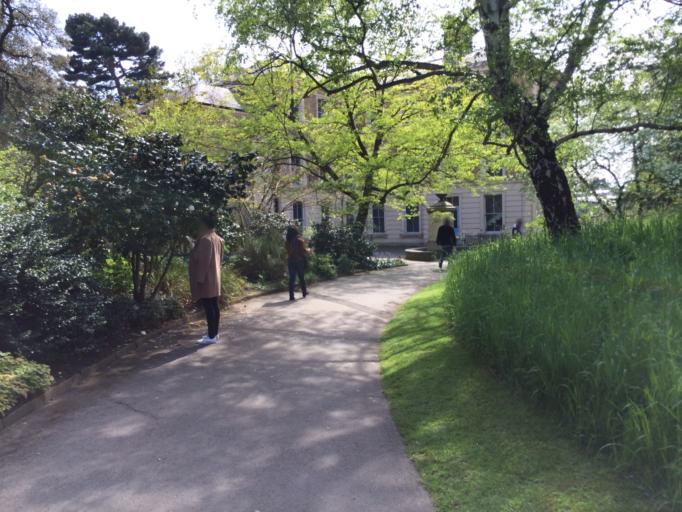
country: GB
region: England
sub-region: Greater London
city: Brentford
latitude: 51.4801
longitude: -0.2896
